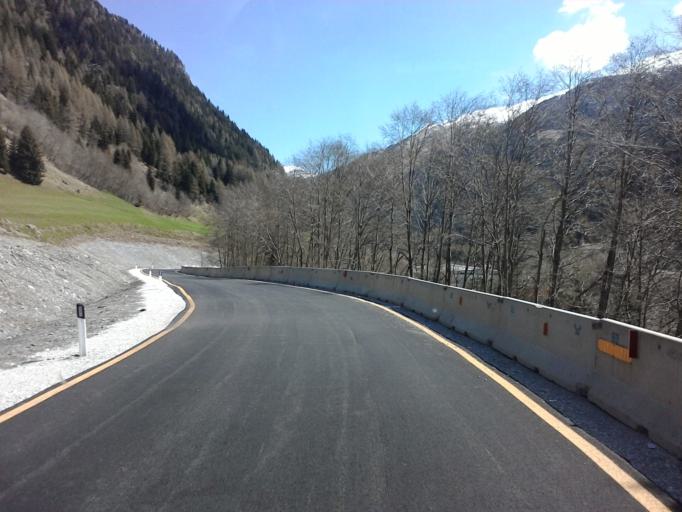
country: IT
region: Trentino-Alto Adige
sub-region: Bolzano
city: Colle Isarco
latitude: 46.9755
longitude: 11.4772
